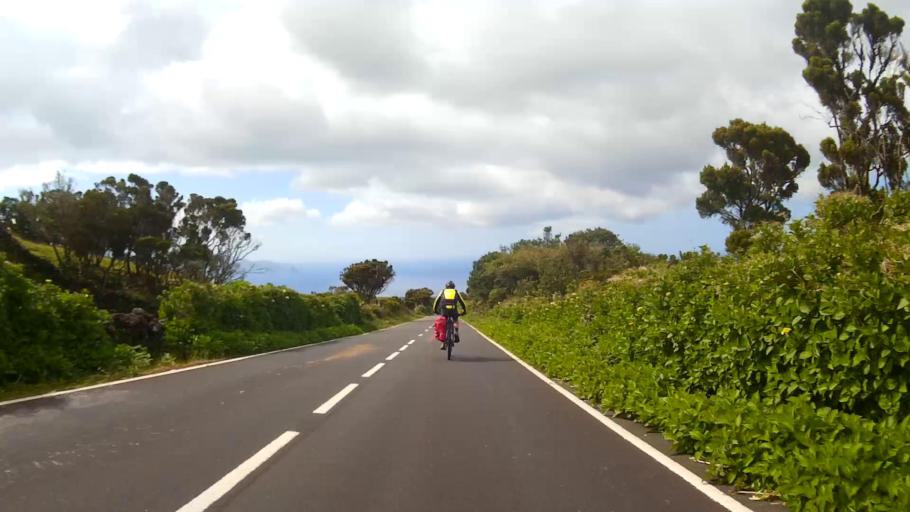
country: PT
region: Azores
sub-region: Madalena
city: Madalena
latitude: 38.4974
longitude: -28.4613
